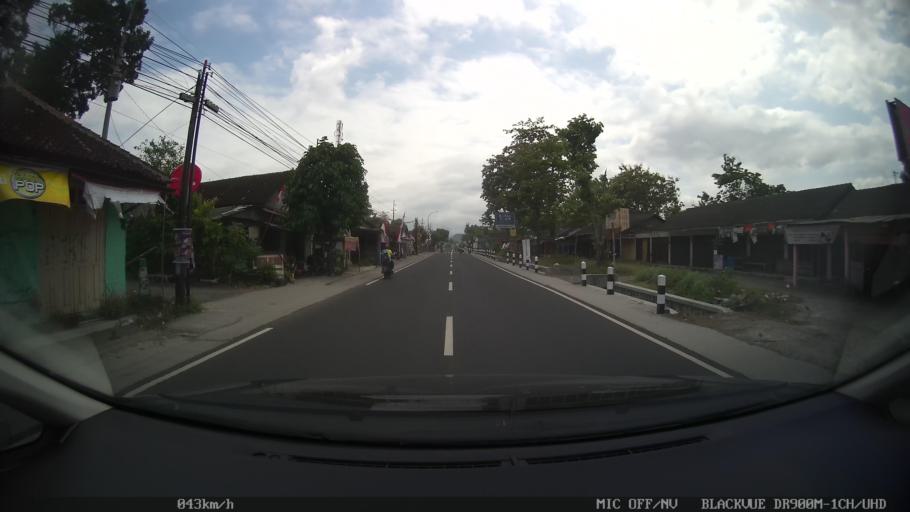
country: ID
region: Central Java
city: Candi Prambanan
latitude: -7.8018
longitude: 110.4829
